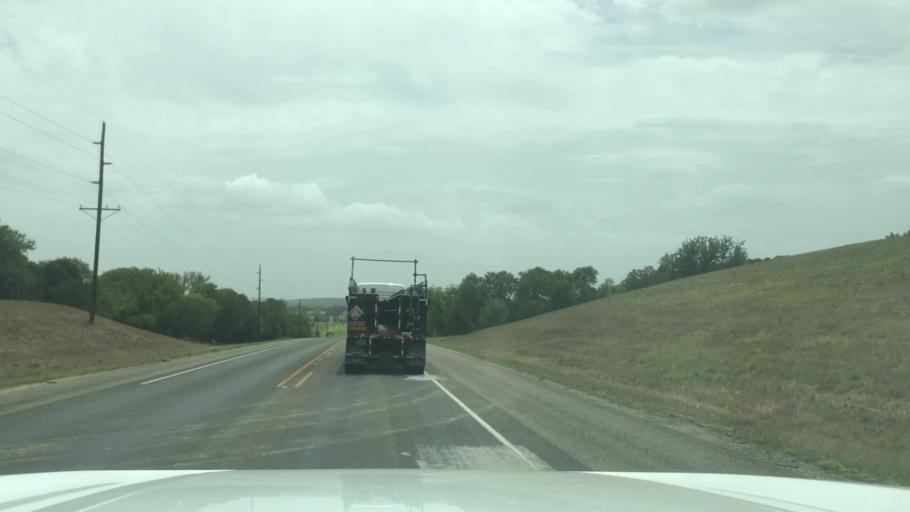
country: US
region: Texas
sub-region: Bosque County
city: Clifton
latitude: 31.7188
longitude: -97.5477
